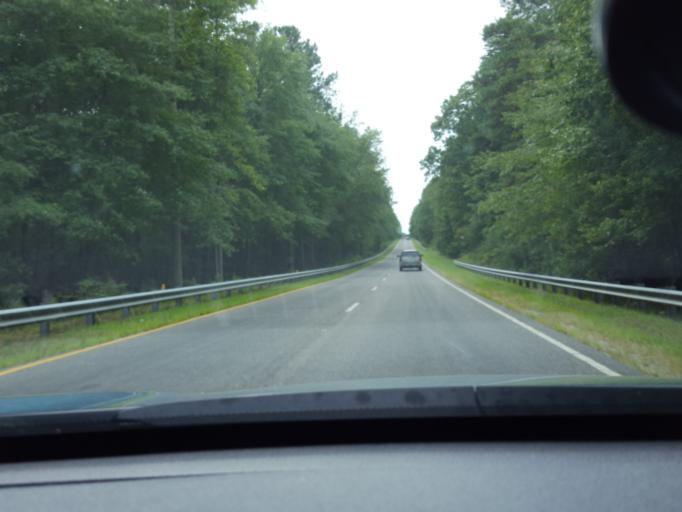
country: US
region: Virginia
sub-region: Caroline County
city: Bowling Green
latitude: 38.0979
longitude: -77.2810
